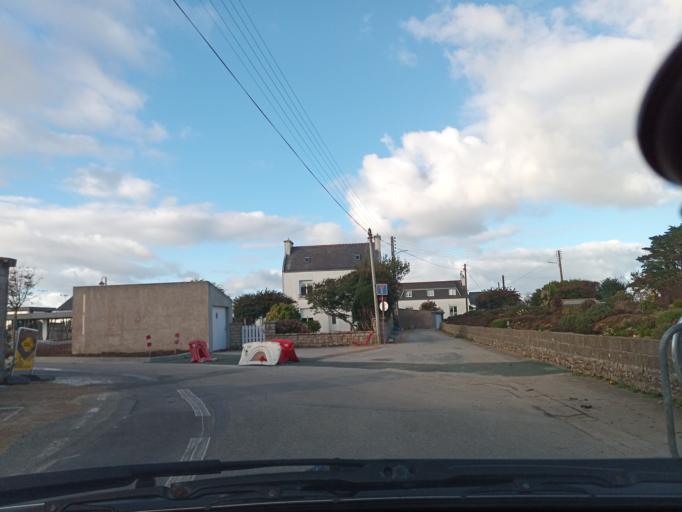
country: FR
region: Brittany
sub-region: Departement du Finistere
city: Plouhinec
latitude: 48.0160
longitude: -4.4906
